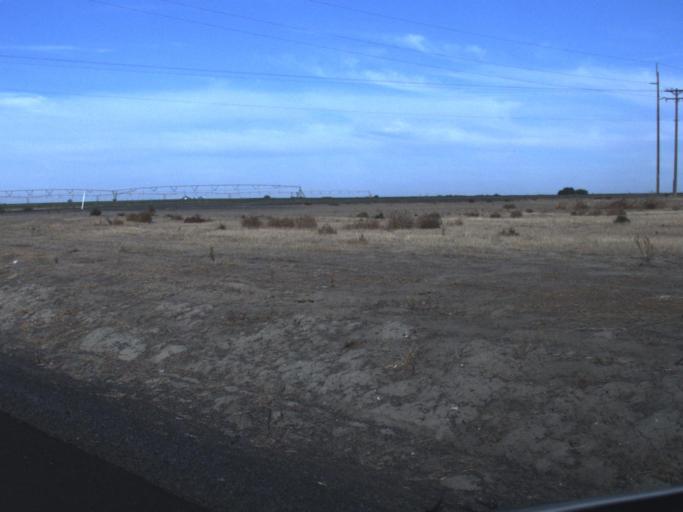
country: US
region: Washington
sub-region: Franklin County
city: Connell
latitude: 46.6635
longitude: -118.9206
